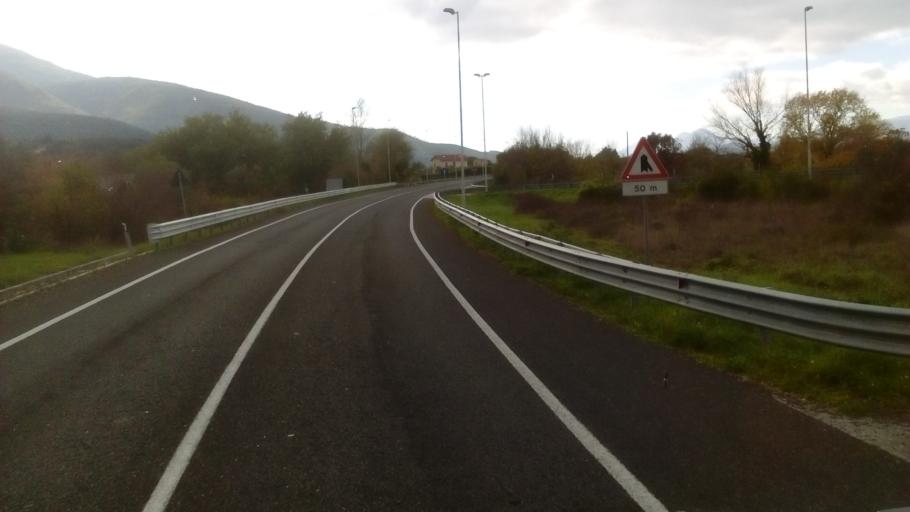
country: IT
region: Molise
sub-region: Provincia di Isernia
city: Sant'Agapito
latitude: 41.5684
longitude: 14.2068
